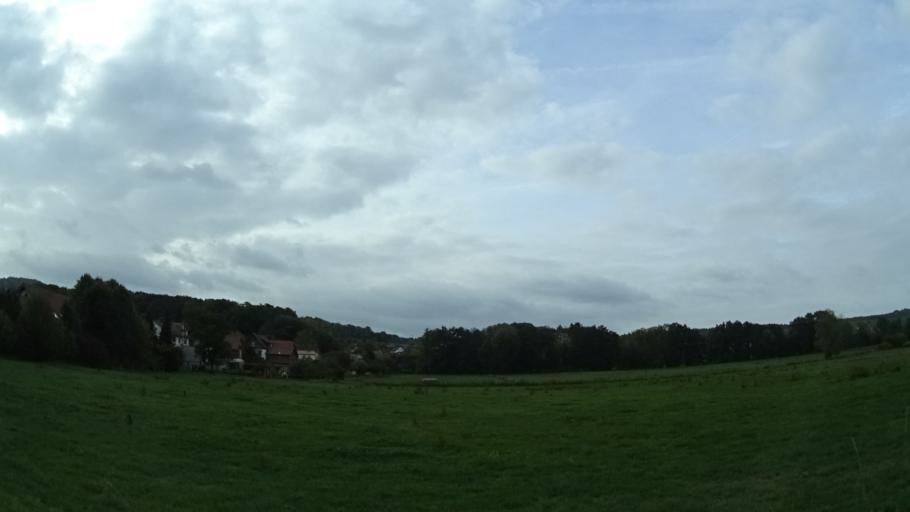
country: DE
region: Hesse
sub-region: Regierungsbezirk Kassel
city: Hofbieber
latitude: 50.5739
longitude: 9.8319
